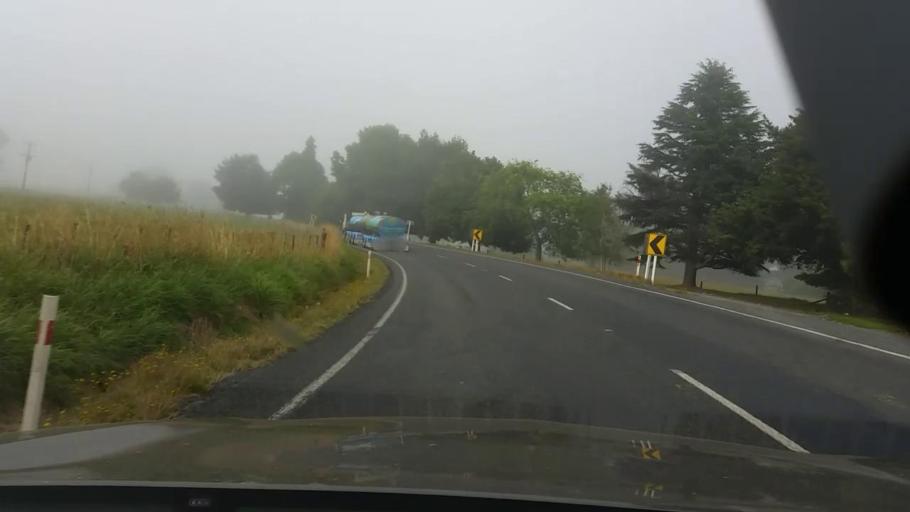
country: NZ
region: Waikato
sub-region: Waikato District
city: Ngaruawahia
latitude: -37.6401
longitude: 175.2950
